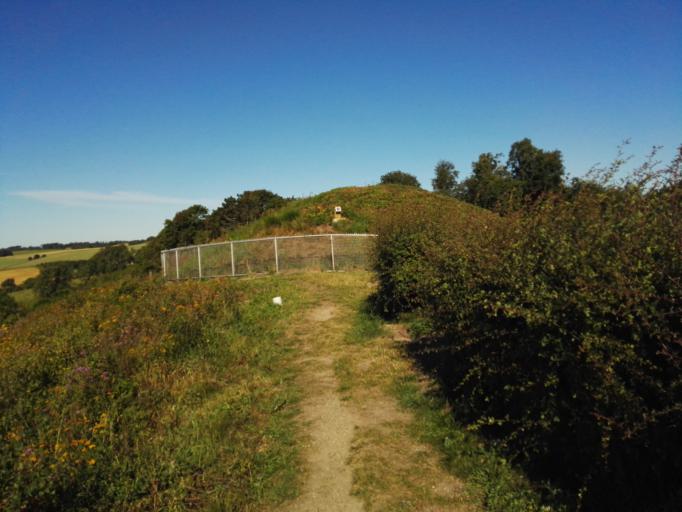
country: DK
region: Zealand
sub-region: Odsherred Kommune
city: Asnaes
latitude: 55.8362
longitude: 11.4837
